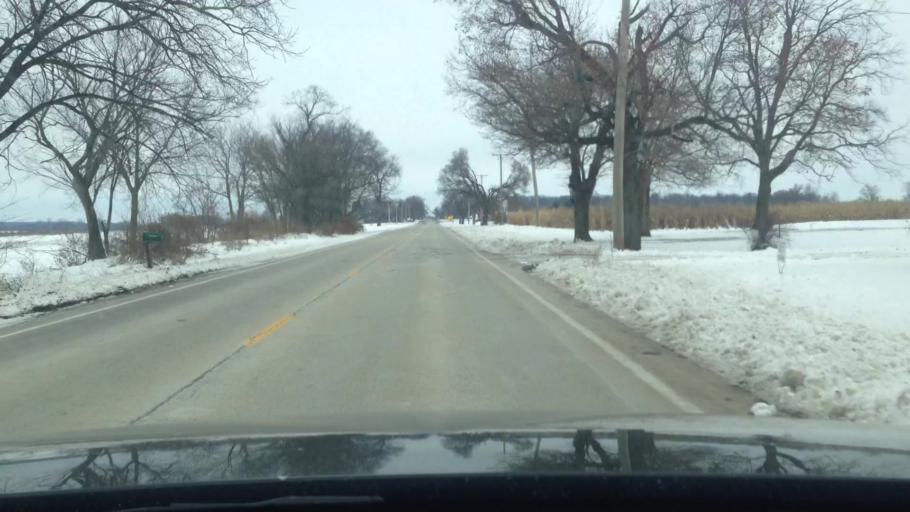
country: US
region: Illinois
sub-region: McHenry County
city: Hebron
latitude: 42.4091
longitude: -88.4381
